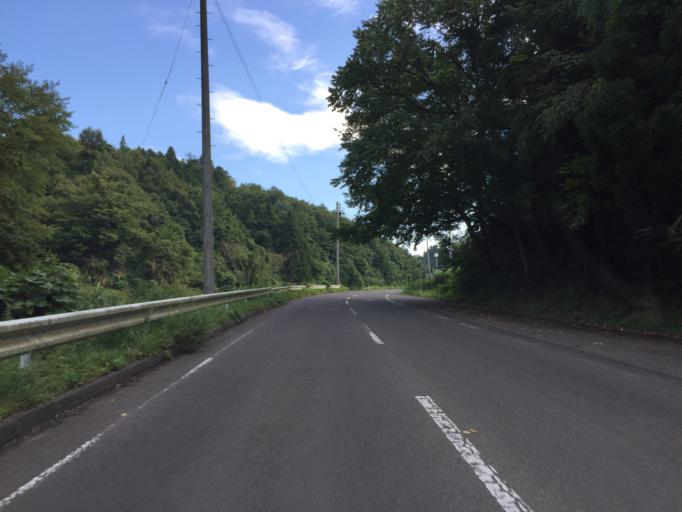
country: JP
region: Fukushima
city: Fukushima-shi
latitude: 37.6607
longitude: 140.5717
